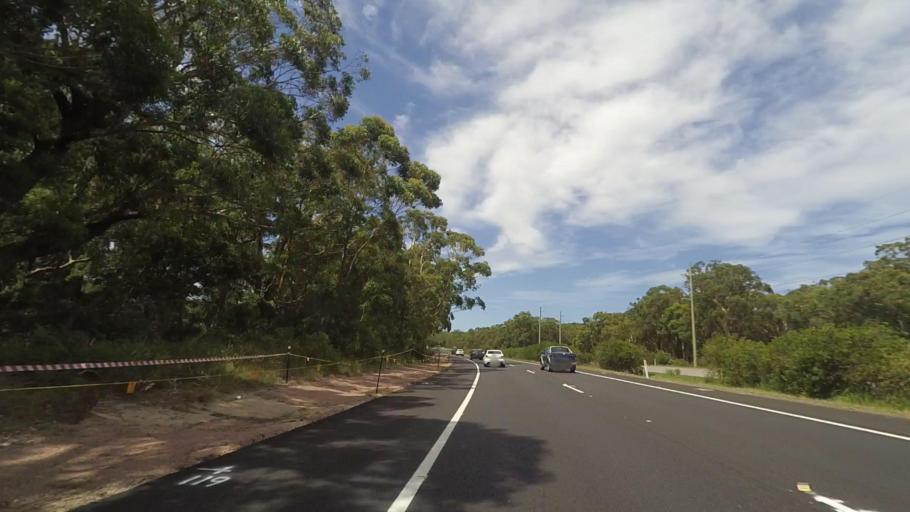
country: AU
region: New South Wales
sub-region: Port Stephens Shire
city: Anna Bay
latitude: -32.7780
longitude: 152.0027
